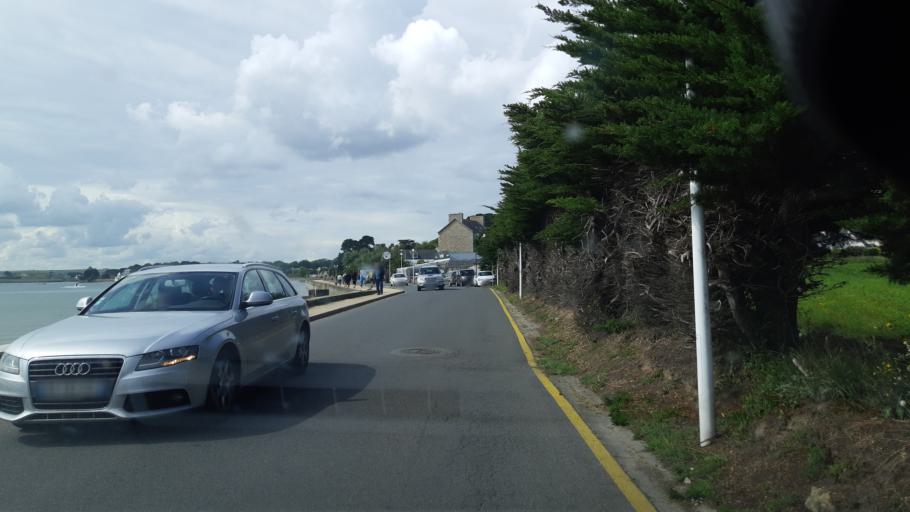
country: FR
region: Brittany
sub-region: Departement du Finistere
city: Saint-Pol-de-Leon
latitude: 48.6901
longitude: -3.9683
